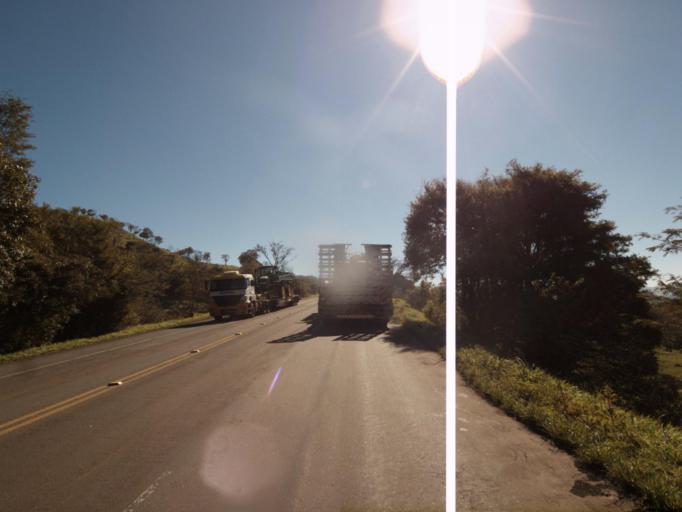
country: BR
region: Rio Grande do Sul
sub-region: Frederico Westphalen
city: Frederico Westphalen
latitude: -26.8247
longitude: -53.4209
